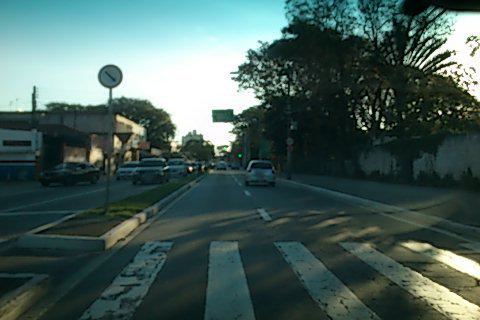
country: BR
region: Sao Paulo
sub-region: Sao Jose Dos Campos
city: Sao Jose dos Campos
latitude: -23.1742
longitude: -45.8848
